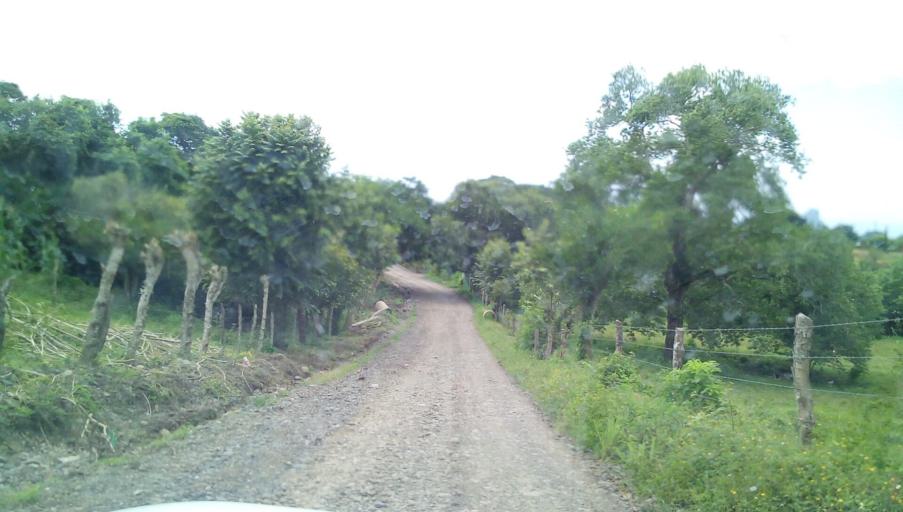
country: MX
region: Veracruz
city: Tepetzintla
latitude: 21.1292
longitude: -97.8540
